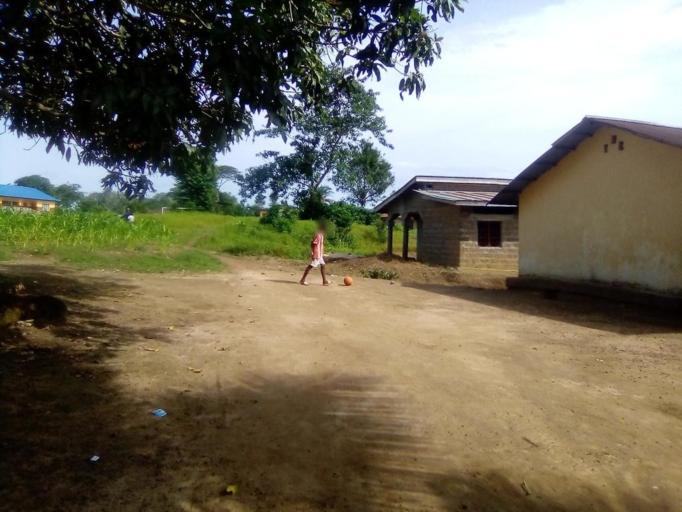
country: SL
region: Southern Province
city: Pujehun
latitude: 7.3639
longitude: -11.7268
